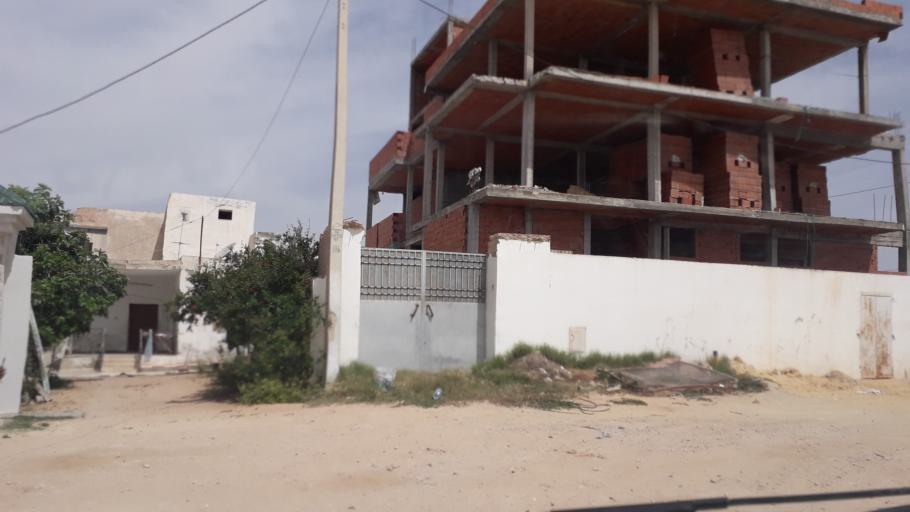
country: TN
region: Safaqis
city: Al Qarmadah
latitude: 34.8035
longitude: 10.7667
